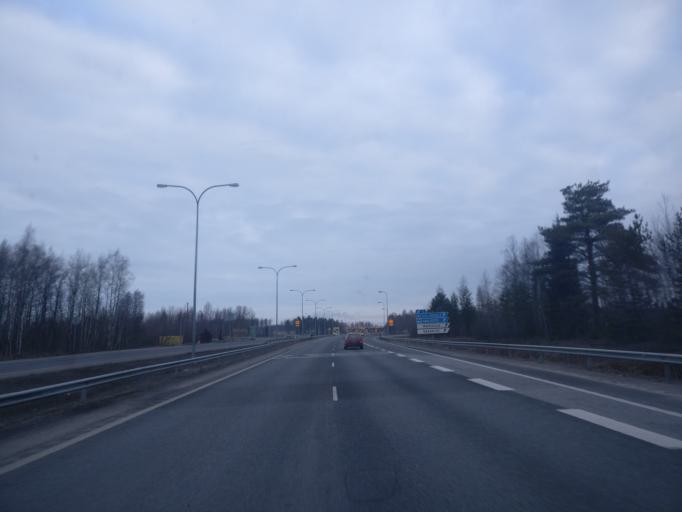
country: FI
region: Northern Ostrobothnia
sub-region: Oulu
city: Kempele
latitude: 64.9541
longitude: 25.5238
